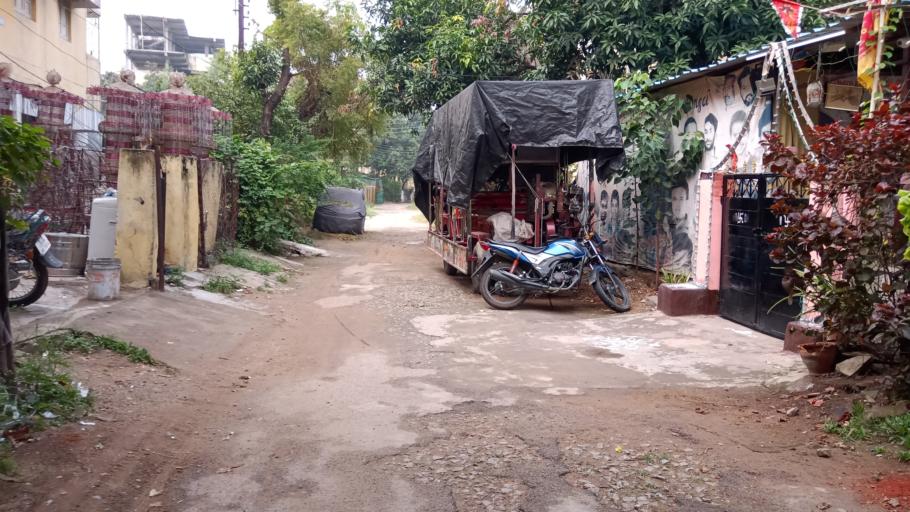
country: IN
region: Telangana
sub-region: Rangareddi
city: Kukatpalli
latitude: 17.4444
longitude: 78.4435
